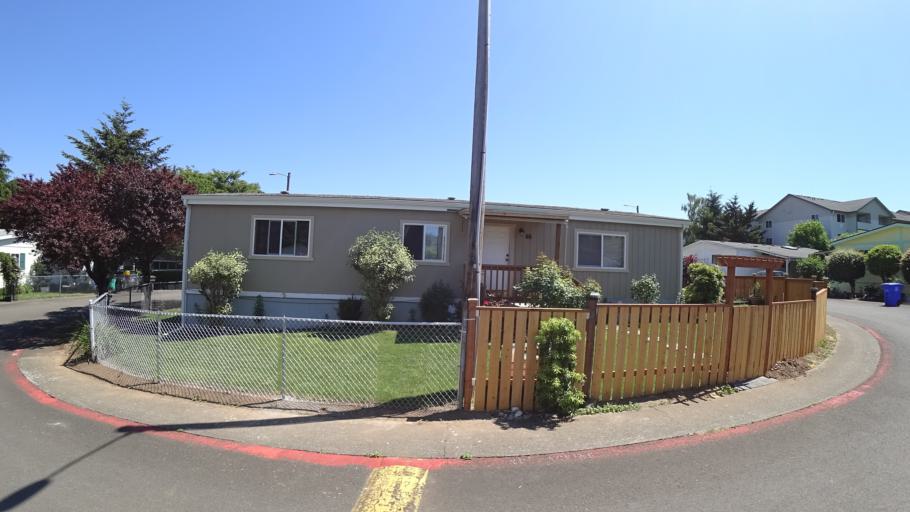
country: US
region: Oregon
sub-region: Clackamas County
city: Happy Valley
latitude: 45.4789
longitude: -122.5309
